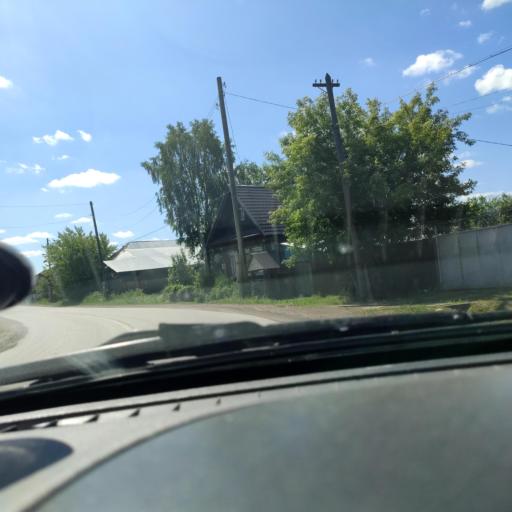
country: RU
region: Perm
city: Kukushtan
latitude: 57.6466
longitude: 56.4938
